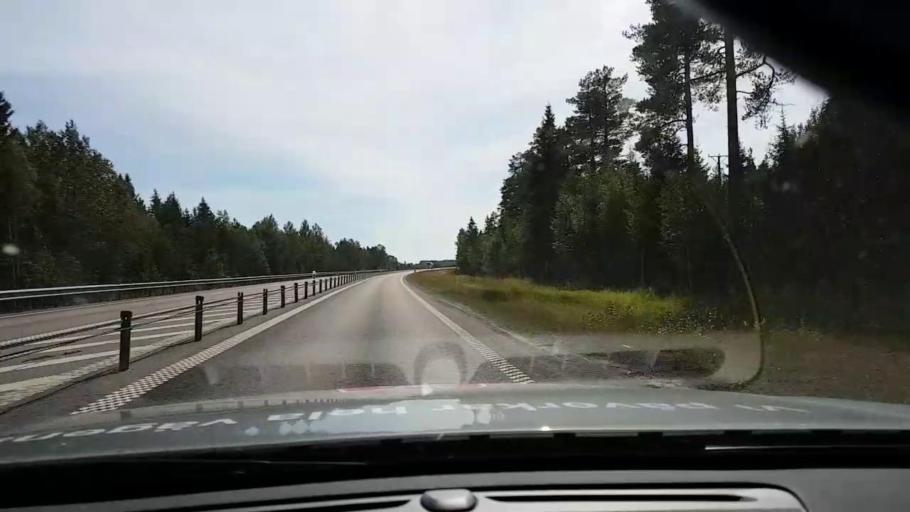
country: SE
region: Vaesternorrland
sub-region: OErnskoeldsviks Kommun
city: Husum
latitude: 63.3735
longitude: 19.1898
